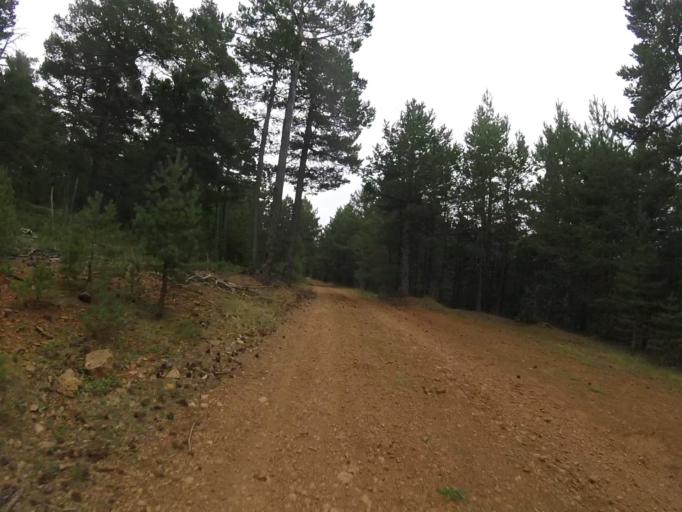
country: ES
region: Aragon
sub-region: Provincia de Teruel
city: Valdelinares
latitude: 40.3668
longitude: -0.6184
